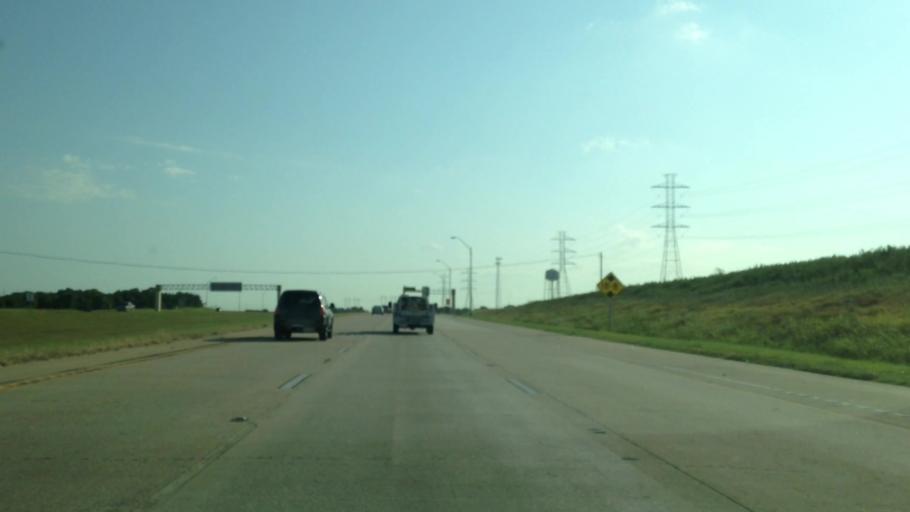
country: US
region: Texas
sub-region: Travis County
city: Hornsby Bend
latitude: 30.2745
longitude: -97.5856
